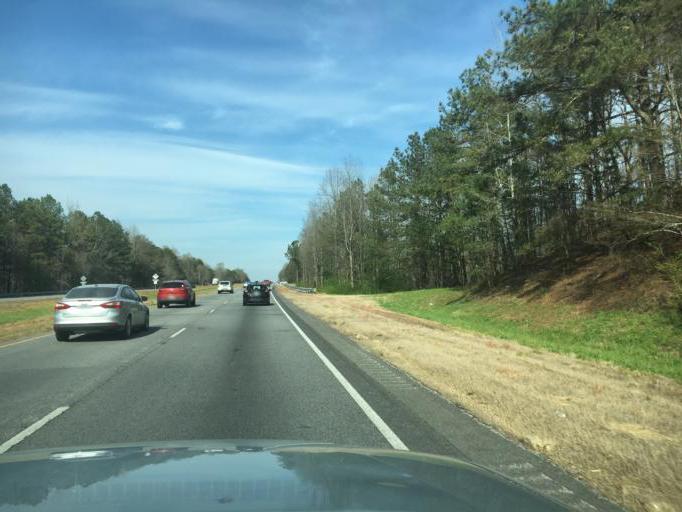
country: US
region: Georgia
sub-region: Hall County
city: Lula
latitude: 34.4029
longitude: -83.6786
